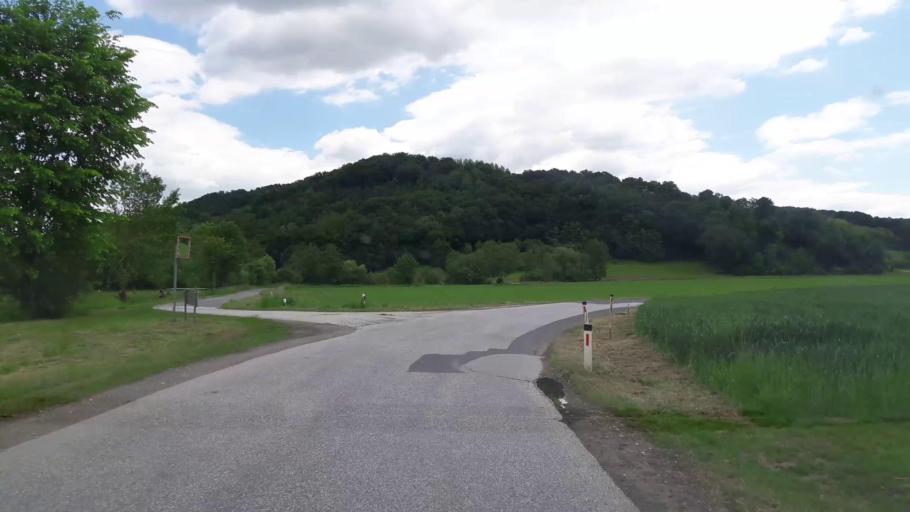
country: AT
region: Styria
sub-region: Politischer Bezirk Hartberg-Fuerstenfeld
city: UEbersbach
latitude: 47.0130
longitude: 16.0494
